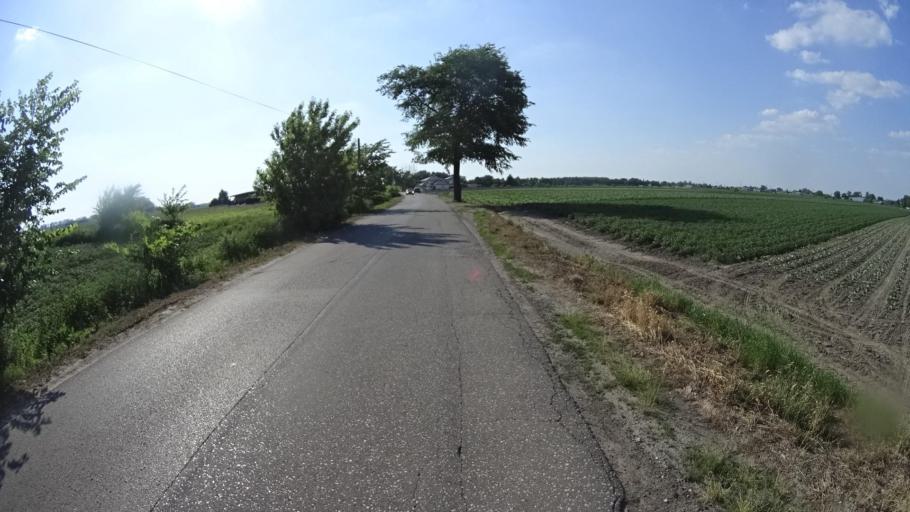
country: PL
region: Masovian Voivodeship
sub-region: Powiat warszawski zachodni
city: Ozarow Mazowiecki
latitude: 52.2024
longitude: 20.7634
